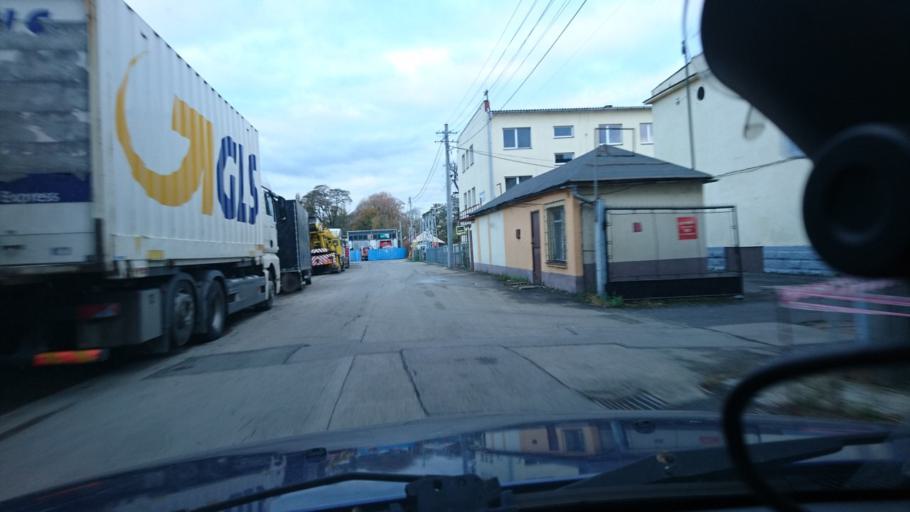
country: PL
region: Silesian Voivodeship
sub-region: Bielsko-Biala
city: Bielsko-Biala
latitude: 49.8337
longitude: 19.0533
